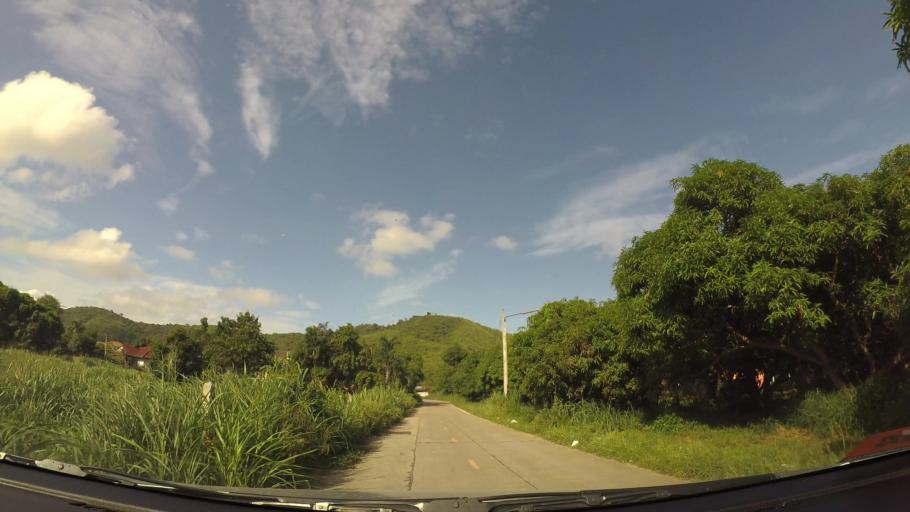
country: TH
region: Chon Buri
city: Sattahip
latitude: 12.6852
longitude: 100.9100
